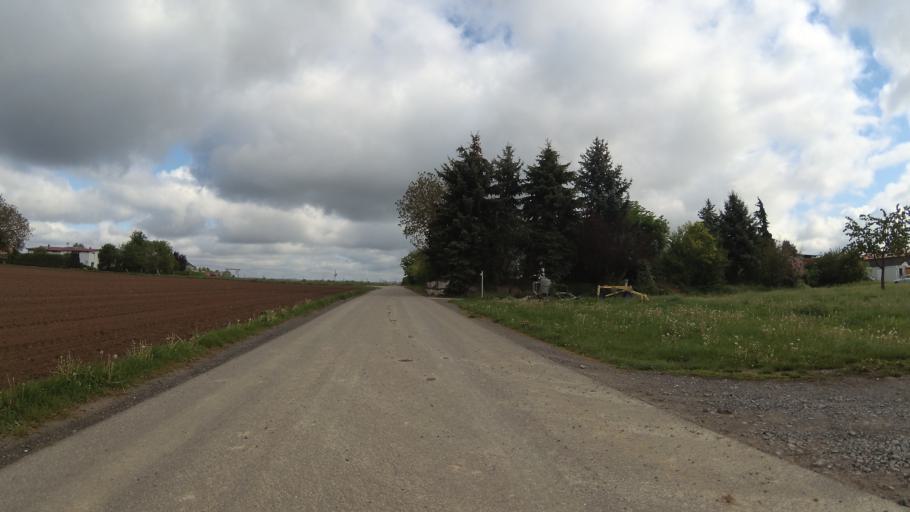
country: DE
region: Baden-Wuerttemberg
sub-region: Regierungsbezirk Stuttgart
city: Oedheim
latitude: 49.2194
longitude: 9.2408
